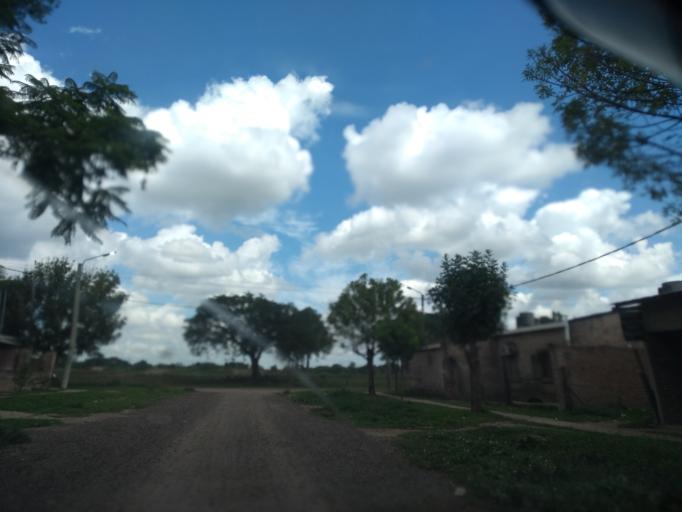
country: AR
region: Chaco
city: Fontana
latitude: -27.4061
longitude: -59.0365
